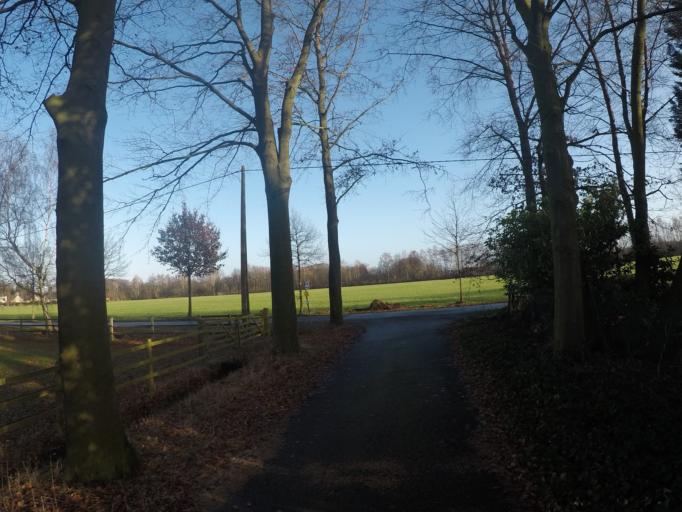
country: BE
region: Flanders
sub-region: Provincie Antwerpen
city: Brasschaat
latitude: 51.2938
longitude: 4.5400
